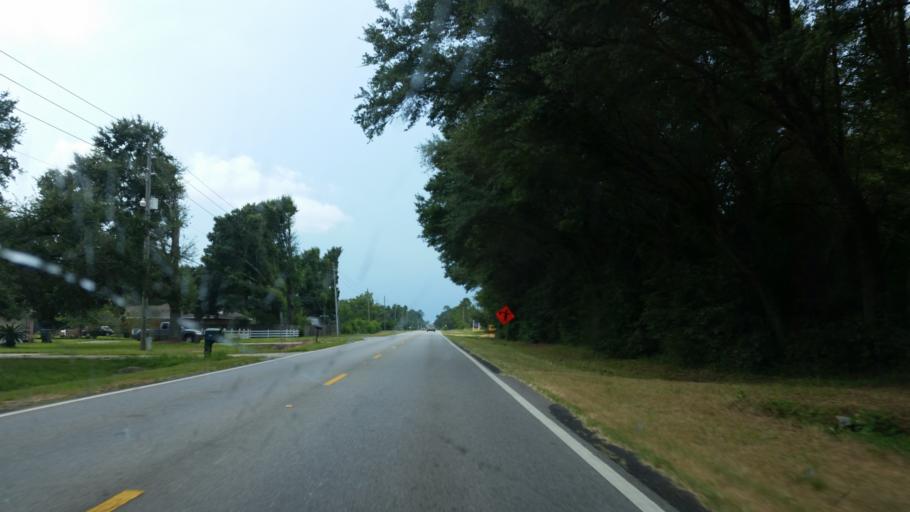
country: US
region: Florida
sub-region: Santa Rosa County
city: Pace
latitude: 30.6286
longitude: -87.1674
